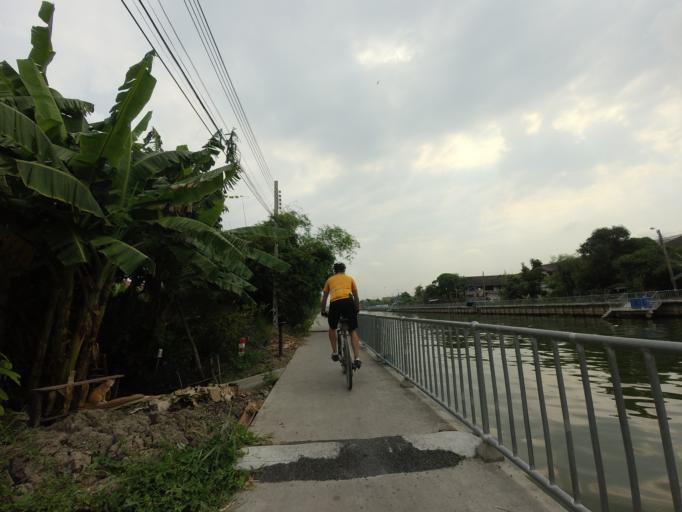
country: TH
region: Bangkok
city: Suan Luang
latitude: 13.7193
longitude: 100.6551
